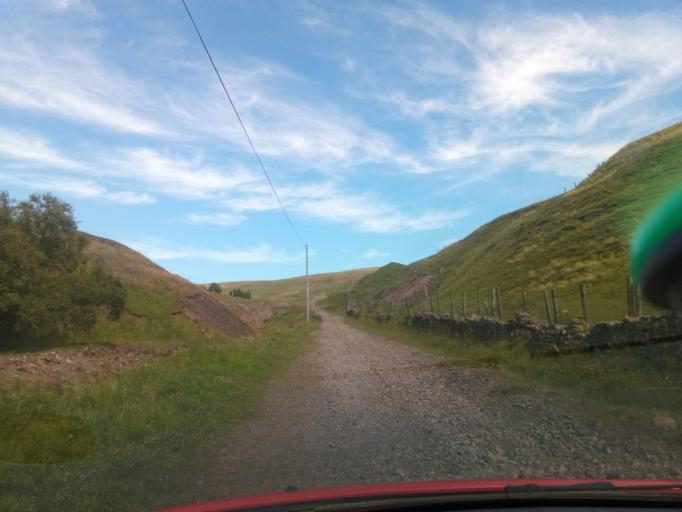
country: GB
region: England
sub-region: County Durham
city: Newbiggin
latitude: 54.7620
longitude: -2.2227
